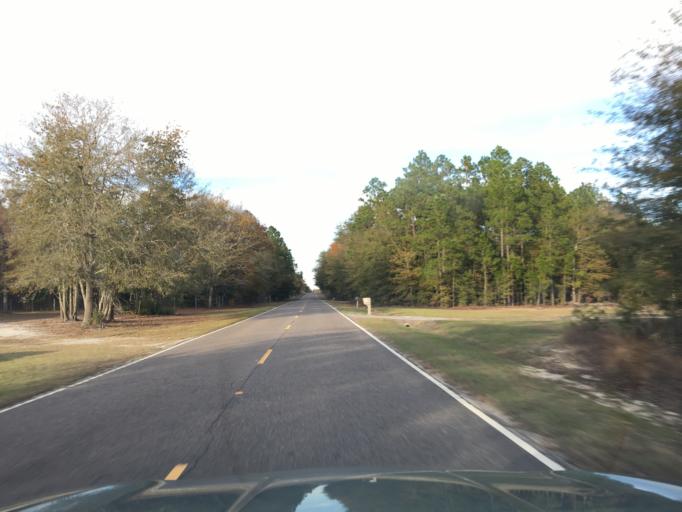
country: US
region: South Carolina
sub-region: Lexington County
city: Red Bank
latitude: 33.6928
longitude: -81.3622
